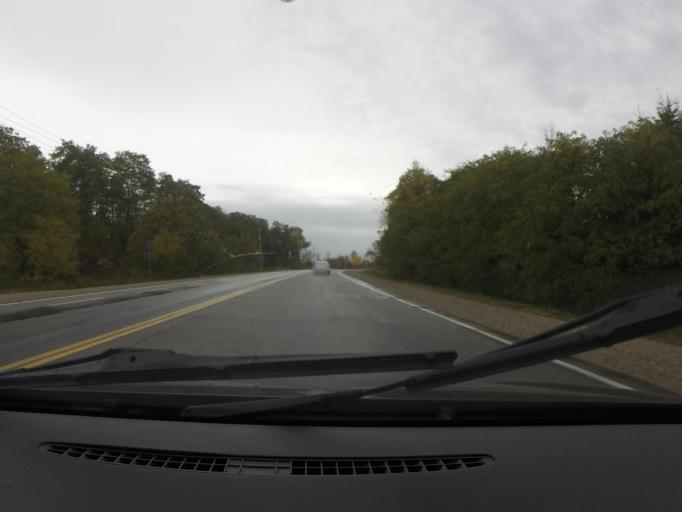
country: CA
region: Ontario
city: Carleton Place
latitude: 45.0459
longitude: -76.2497
